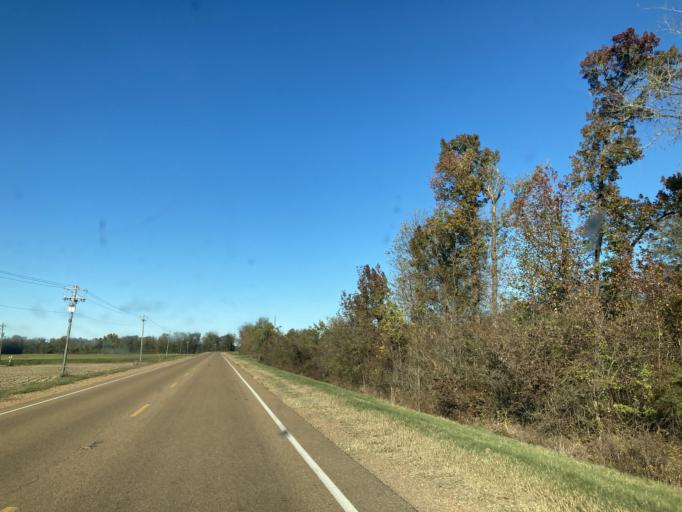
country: US
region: Mississippi
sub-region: Yazoo County
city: Yazoo City
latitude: 32.8097
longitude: -90.4533
